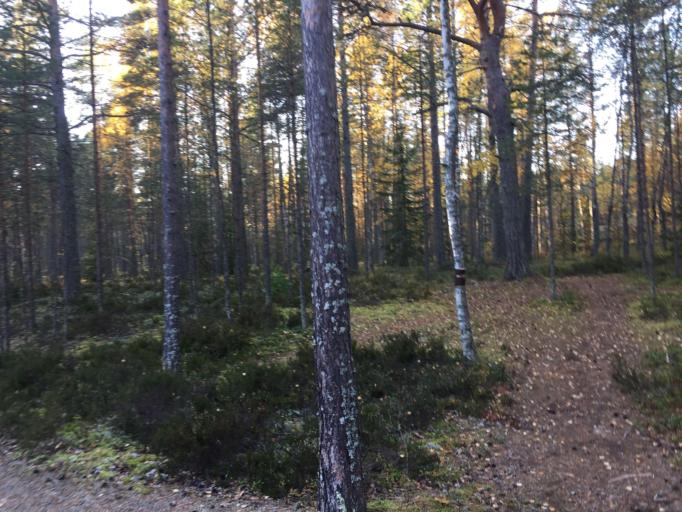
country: RU
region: Republic of Karelia
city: Lakhdenpokh'ya
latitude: 61.2865
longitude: 30.1333
